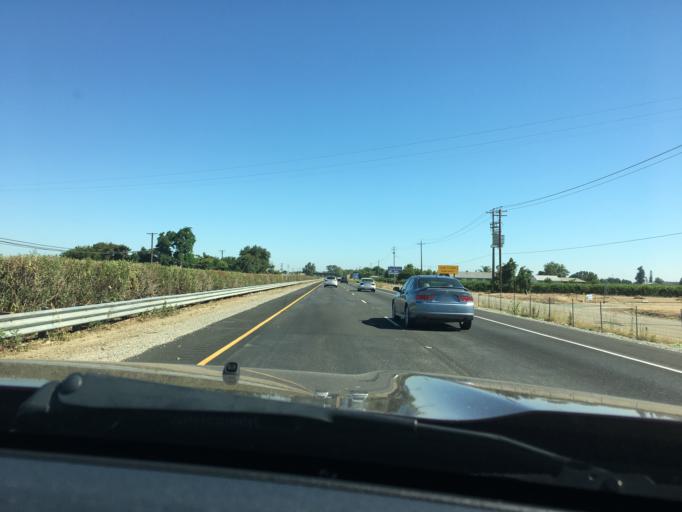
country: US
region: California
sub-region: San Joaquin County
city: Collierville
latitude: 38.1957
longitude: -121.2628
